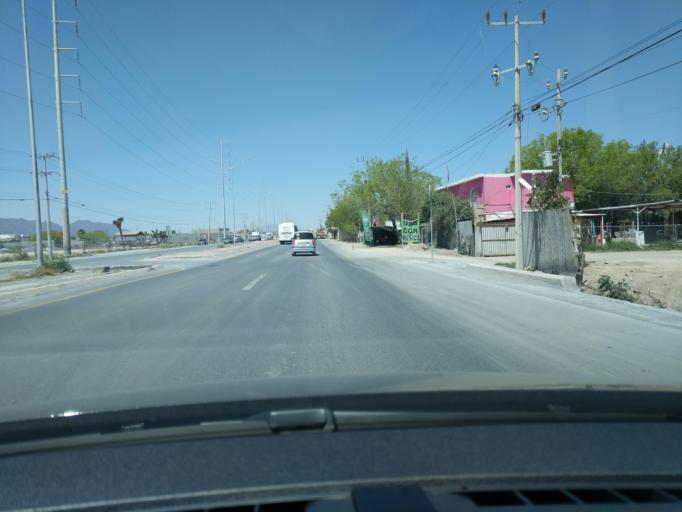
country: MX
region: Nuevo Leon
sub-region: Salinas Victoria
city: Emiliano Zapata
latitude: 25.9075
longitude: -100.2654
